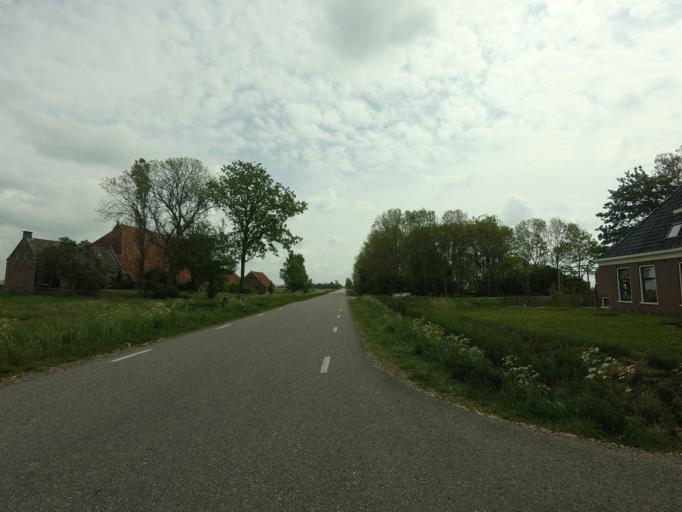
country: NL
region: Friesland
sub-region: Sudwest Fryslan
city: Bolsward
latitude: 53.0987
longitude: 5.5231
